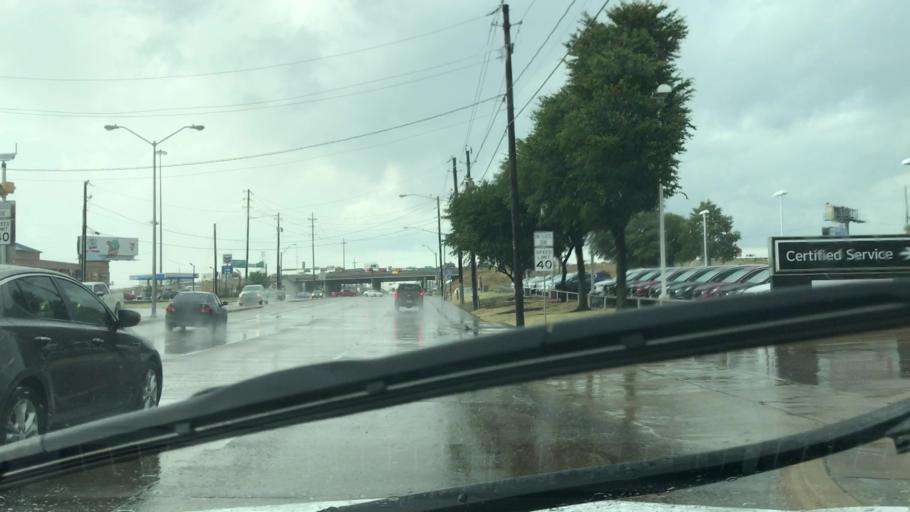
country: US
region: Texas
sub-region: Dallas County
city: Garland
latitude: 32.8723
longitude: -96.6830
